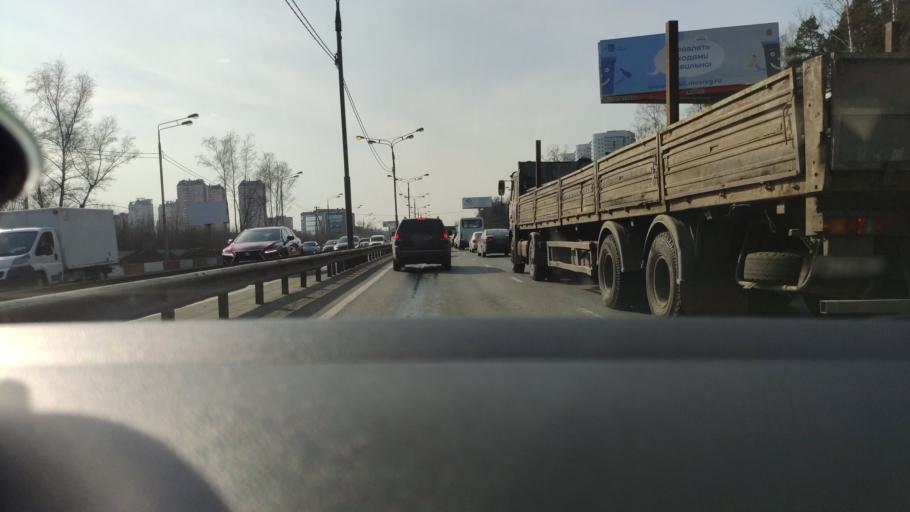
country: RU
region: Moskovskaya
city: Balashikha
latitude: 55.8011
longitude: 38.0028
